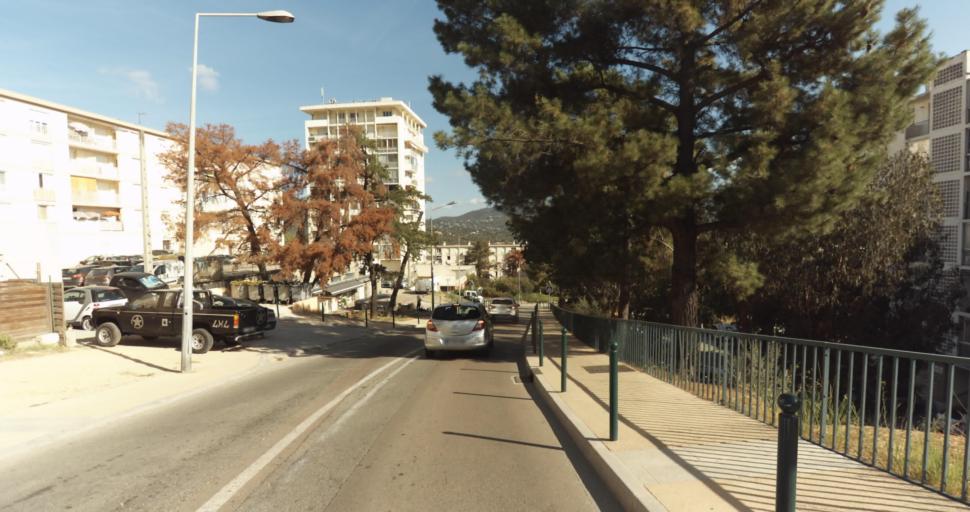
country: FR
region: Corsica
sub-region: Departement de la Corse-du-Sud
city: Ajaccio
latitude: 41.9257
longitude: 8.7287
